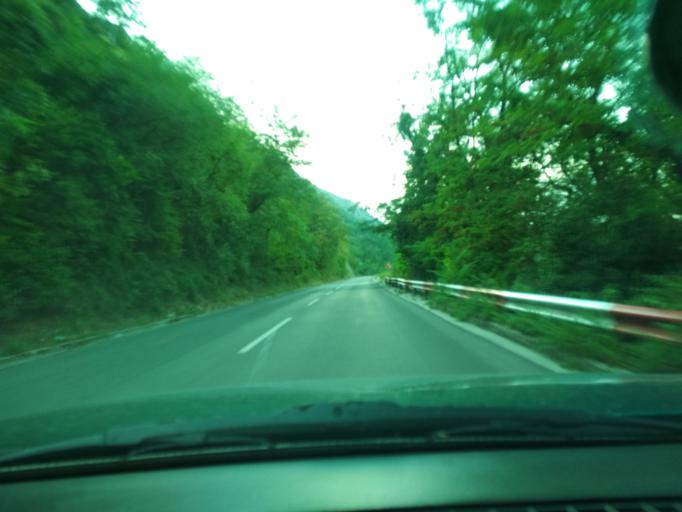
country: ME
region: Kotor
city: Kotor
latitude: 42.4168
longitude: 18.7600
